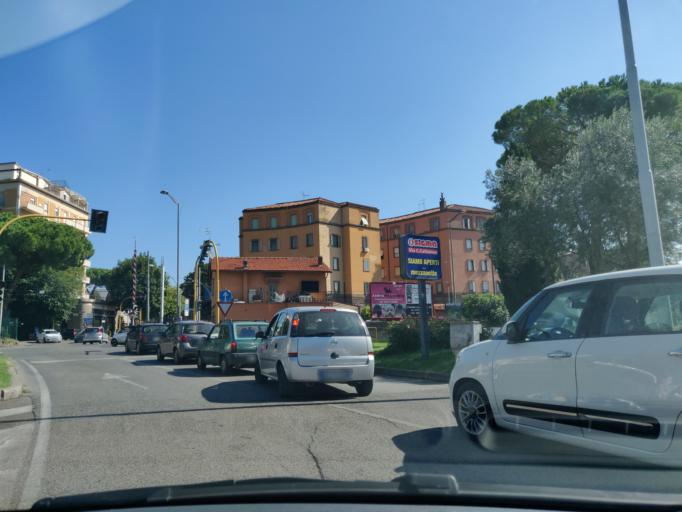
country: IT
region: Latium
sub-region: Provincia di Viterbo
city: Viterbo
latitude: 42.4230
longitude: 12.1069
